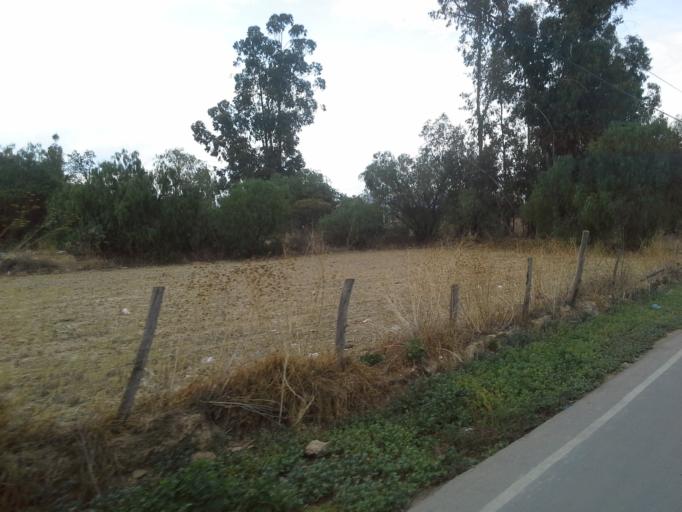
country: BO
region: Cochabamba
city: Tarata
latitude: -17.5822
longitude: -66.0160
